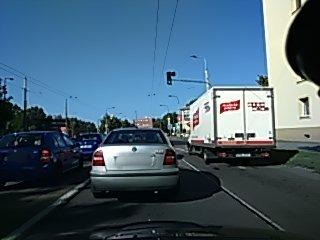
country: CZ
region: Pardubicky
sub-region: Okres Pardubice
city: Pardubice
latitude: 50.0342
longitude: 15.7614
